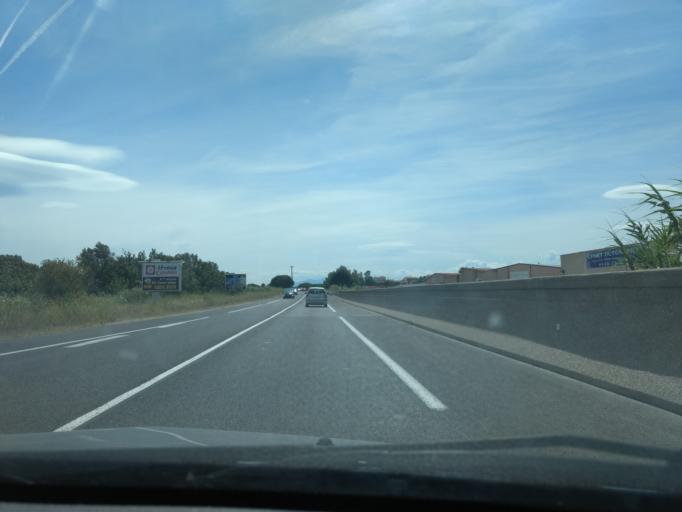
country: FR
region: Languedoc-Roussillon
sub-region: Departement des Pyrenees-Orientales
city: Canet-en-Roussillon
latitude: 42.7077
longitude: 3.0200
